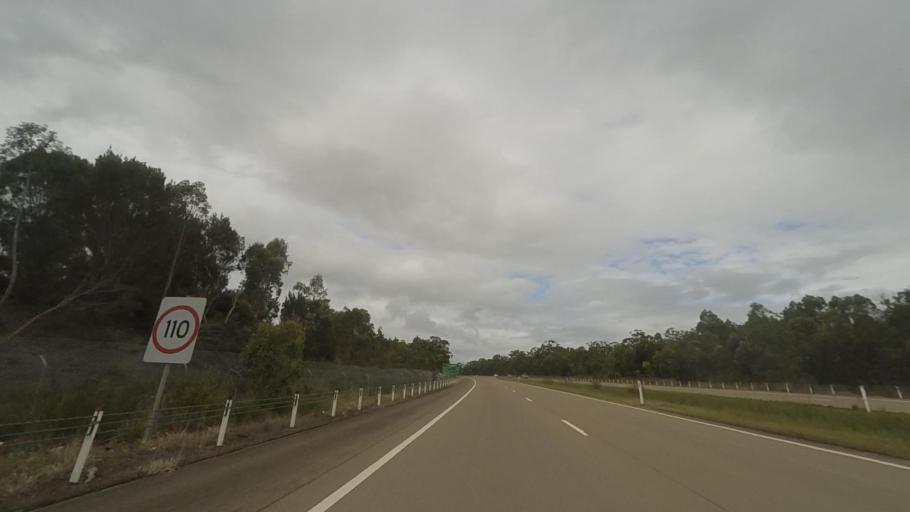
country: AU
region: New South Wales
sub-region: Port Stephens Shire
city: Medowie
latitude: -32.6459
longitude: 151.9233
